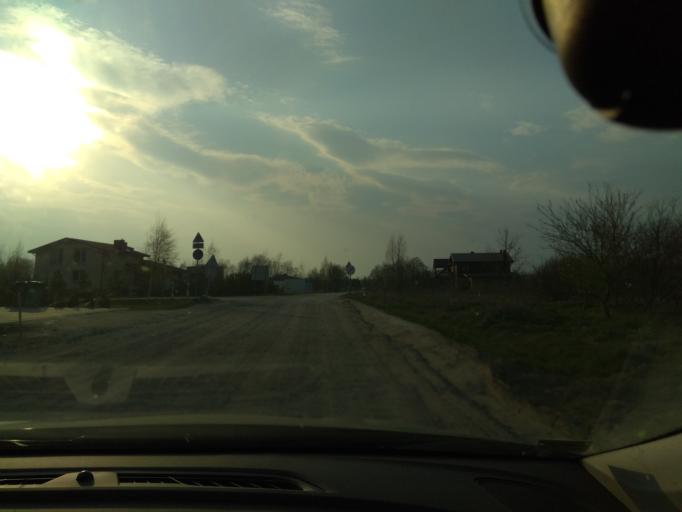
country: LT
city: Baltoji Voke
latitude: 54.5929
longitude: 25.1567
